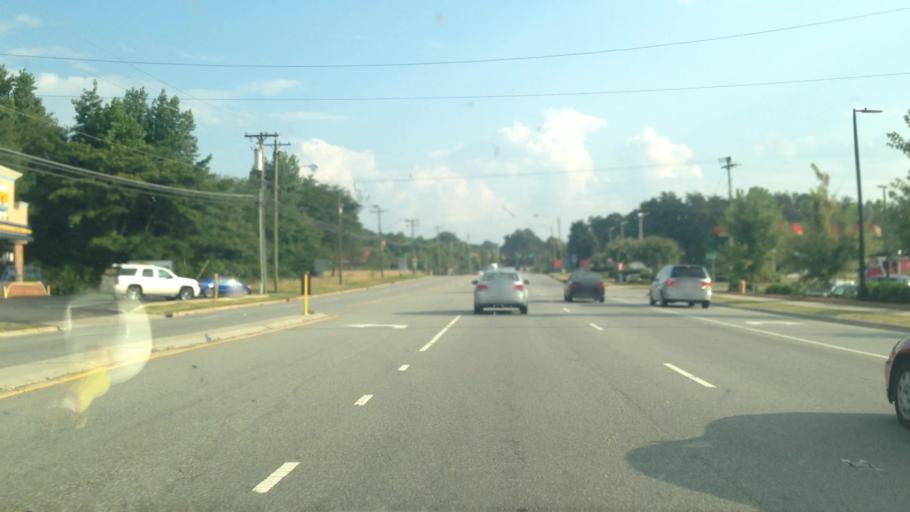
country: US
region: North Carolina
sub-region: Forsyth County
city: Kernersville
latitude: 36.0893
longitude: -80.0626
